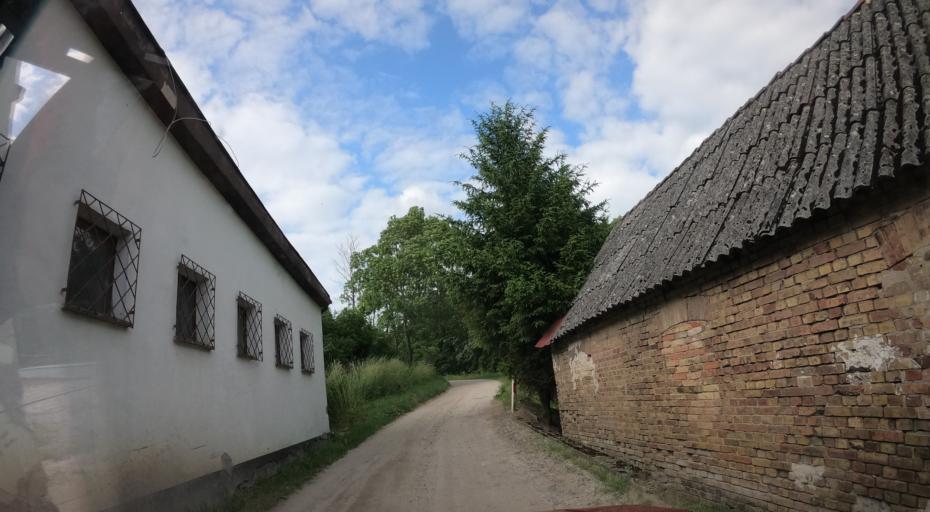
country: PL
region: Lubusz
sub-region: Powiat gorzowski
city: Santok
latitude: 52.7360
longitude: 15.3968
